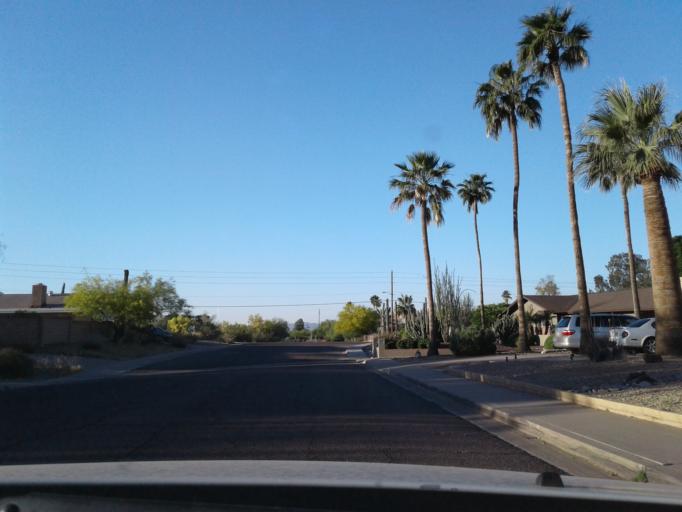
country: US
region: Arizona
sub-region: Maricopa County
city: Phoenix
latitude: 33.5355
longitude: -112.0388
